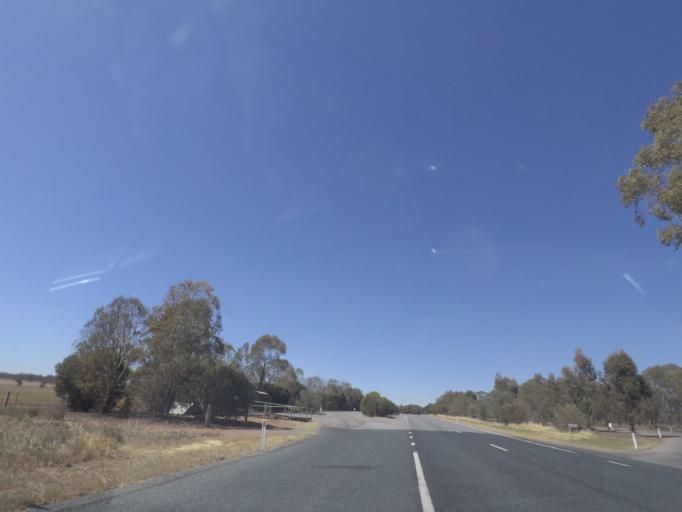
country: AU
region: New South Wales
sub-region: Narrandera
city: Narrandera
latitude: -34.4464
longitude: 146.8396
